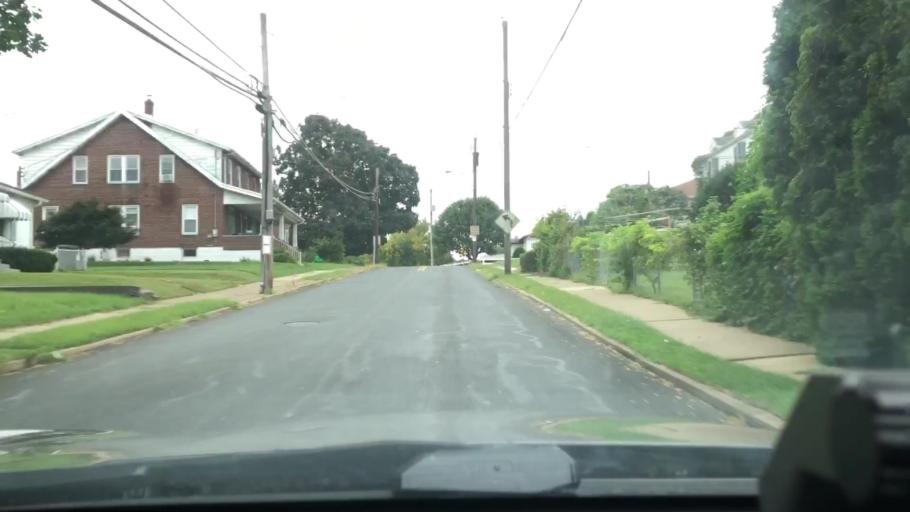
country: US
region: Pennsylvania
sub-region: Lehigh County
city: Fullerton
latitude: 40.6169
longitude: -75.4453
